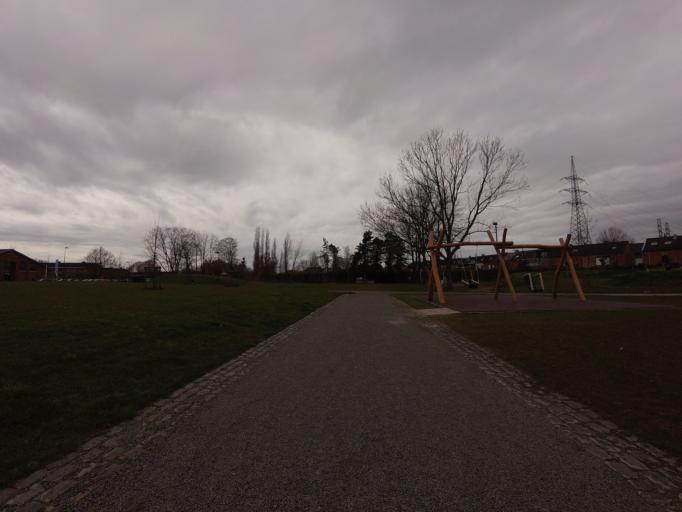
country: BE
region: Flanders
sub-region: Provincie Antwerpen
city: Lier
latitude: 51.1322
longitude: 4.5583
